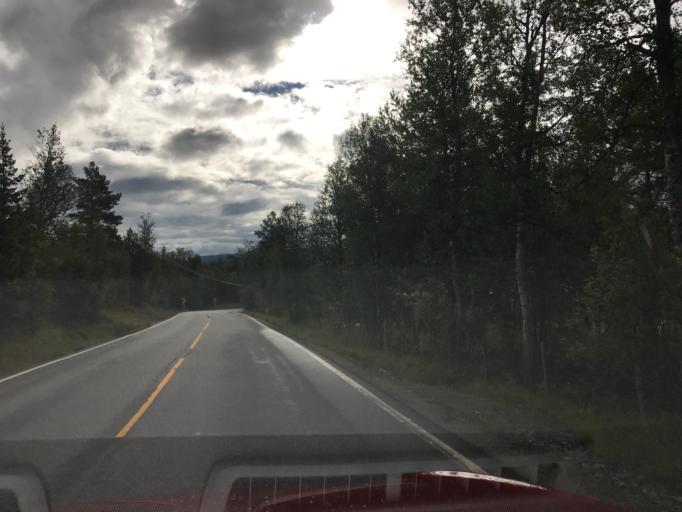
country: NO
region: Buskerud
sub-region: Hol
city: Hol
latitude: 60.4120
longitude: 8.4377
